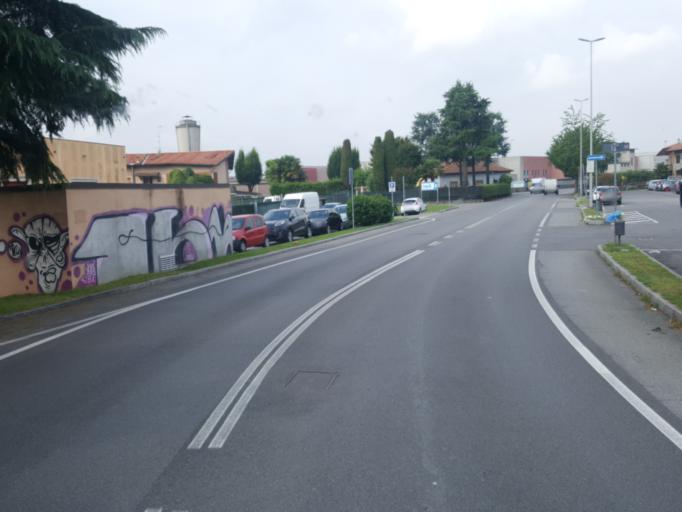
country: IT
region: Lombardy
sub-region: Provincia di Bergamo
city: Grassobbio
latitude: 45.6611
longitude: 9.7276
